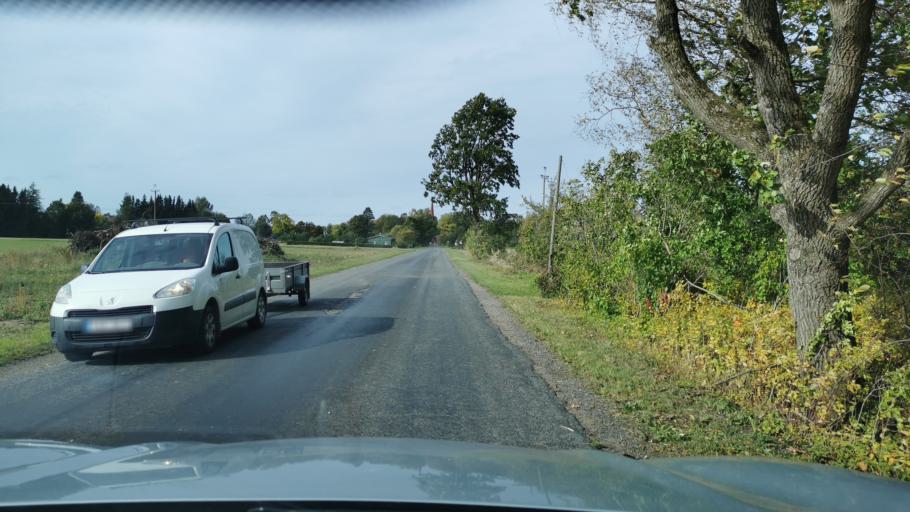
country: EE
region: Laeaene-Virumaa
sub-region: Vinni vald
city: Vinni
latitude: 59.2413
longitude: 26.4832
